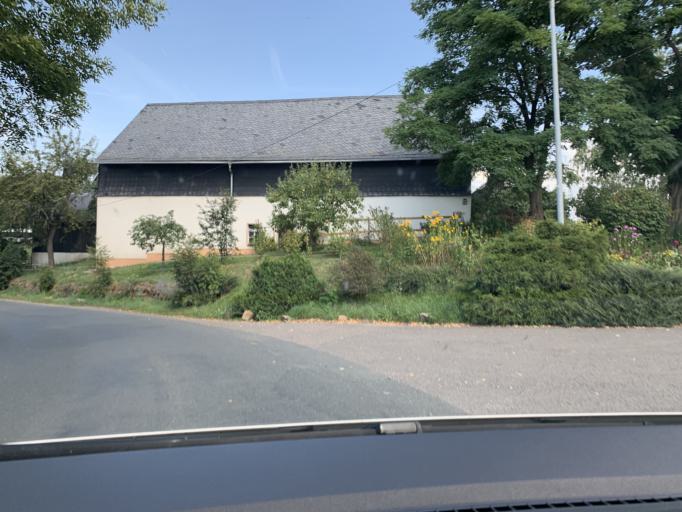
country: DE
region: Saxony
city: Frankenberg
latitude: 50.9201
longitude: 13.0687
